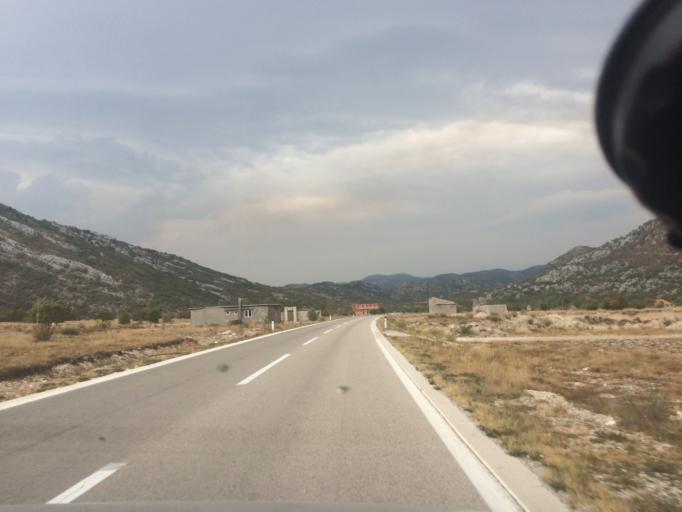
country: ME
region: Kotor
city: Risan
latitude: 42.6127
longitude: 18.6827
